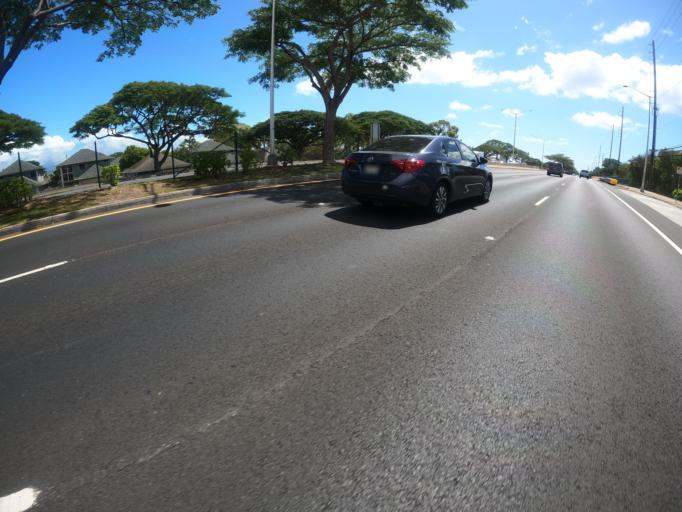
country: US
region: Hawaii
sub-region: Honolulu County
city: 'Ewa Gentry
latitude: 21.3540
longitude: -158.0287
